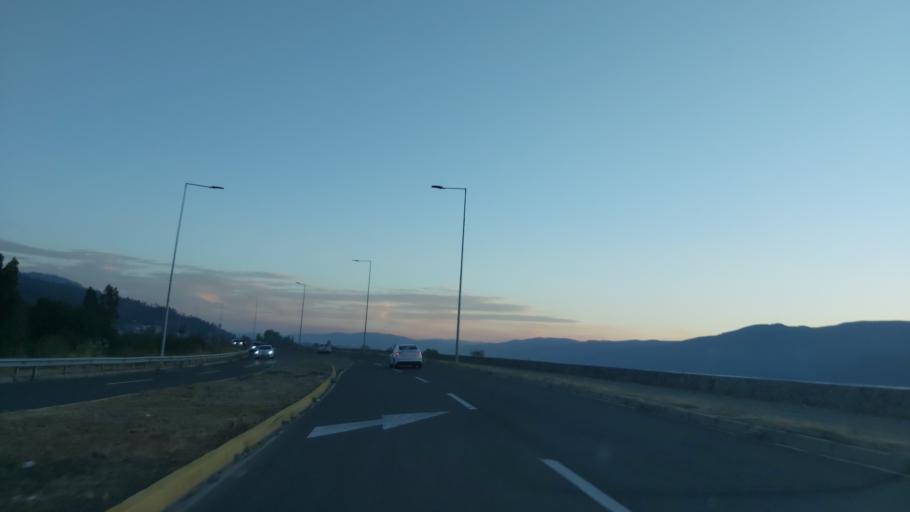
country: CL
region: Biobio
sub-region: Provincia de Concepcion
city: Concepcion
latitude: -36.8705
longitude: -73.0439
